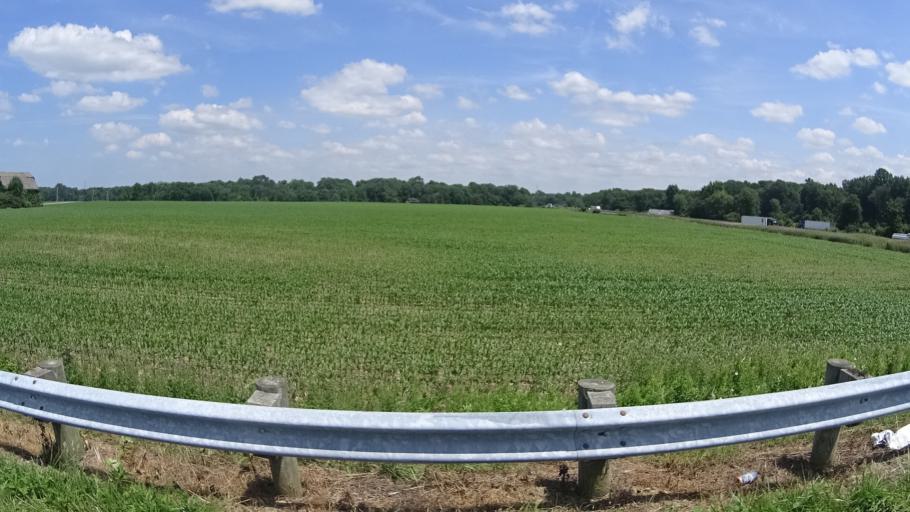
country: US
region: Ohio
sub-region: Erie County
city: Huron
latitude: 41.3264
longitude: -82.5358
